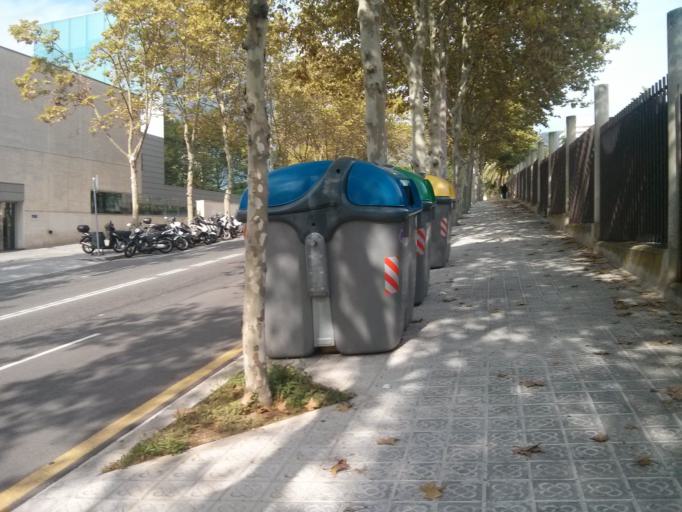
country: ES
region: Catalonia
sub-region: Provincia de Barcelona
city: Esplugues de Llobregat
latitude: 41.3819
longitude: 2.1075
